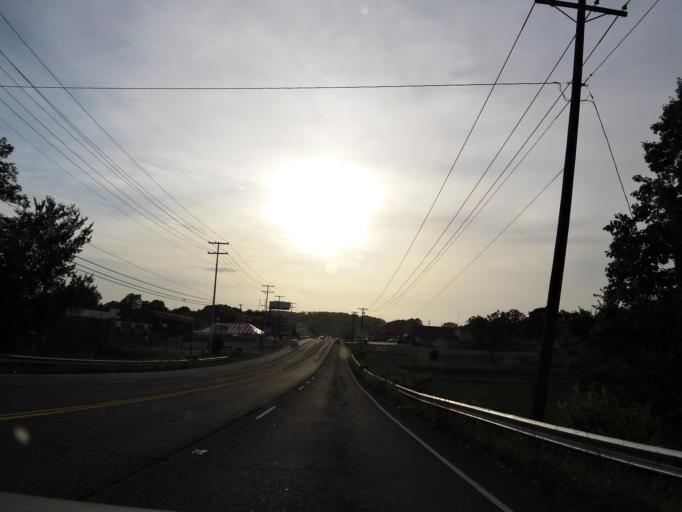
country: US
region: Tennessee
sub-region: Sevier County
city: Seymour
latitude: 35.8814
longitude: -83.7830
